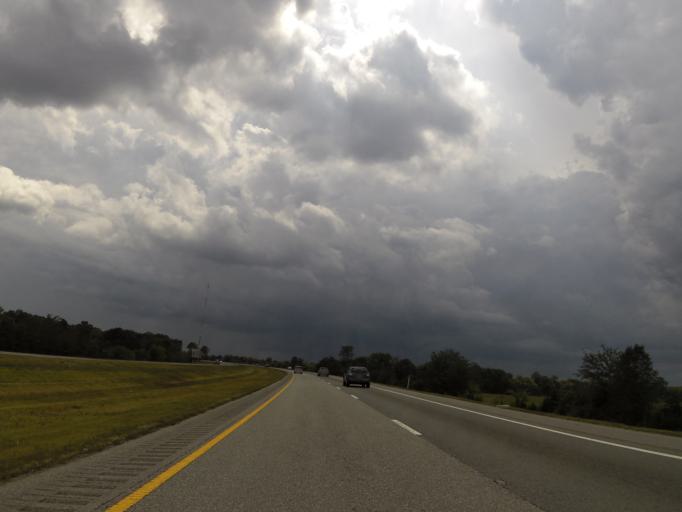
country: US
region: Tennessee
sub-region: Wilson County
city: Rural Hill
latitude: 36.0959
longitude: -86.4229
